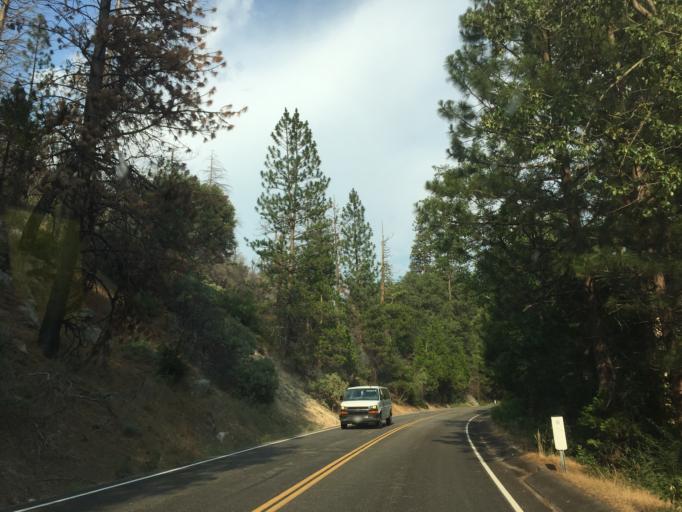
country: US
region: California
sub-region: Tulare County
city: Three Rivers
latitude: 36.8043
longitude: -118.7185
